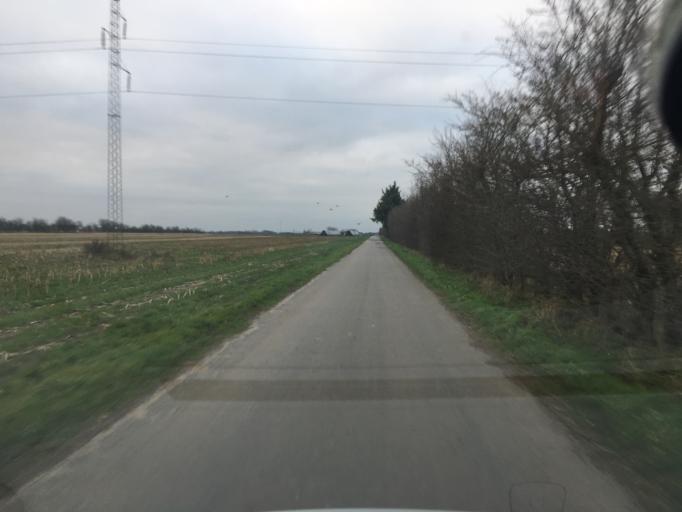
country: DK
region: South Denmark
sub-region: Tonder Kommune
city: Logumkloster
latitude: 55.0519
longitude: 9.0453
